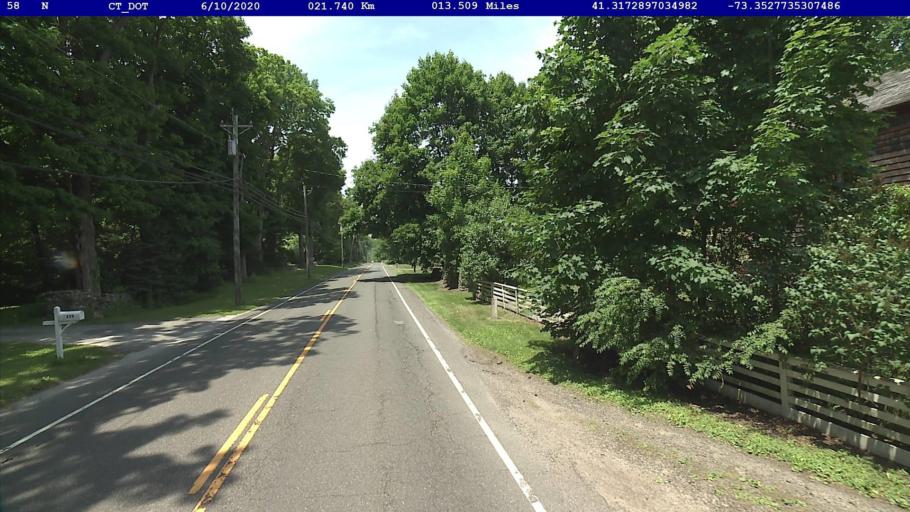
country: US
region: Connecticut
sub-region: Fairfield County
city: Bethel
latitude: 41.3172
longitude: -73.3527
